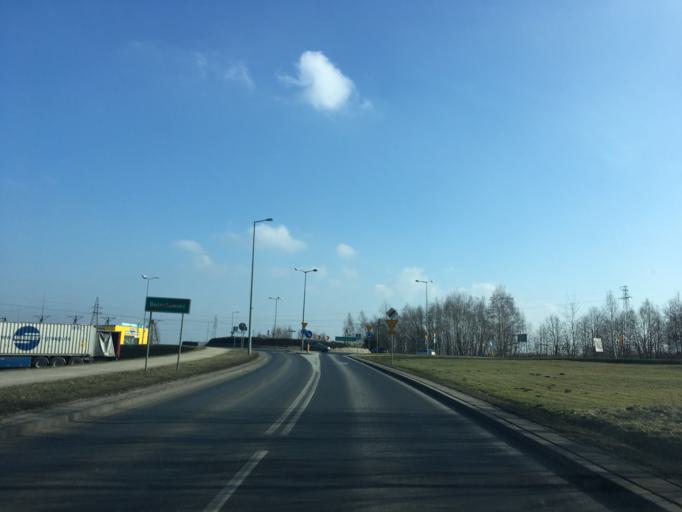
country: PL
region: Lower Silesian Voivodeship
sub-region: Powiat boleslawiecki
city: Boleslawiec
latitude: 51.2618
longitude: 15.5976
